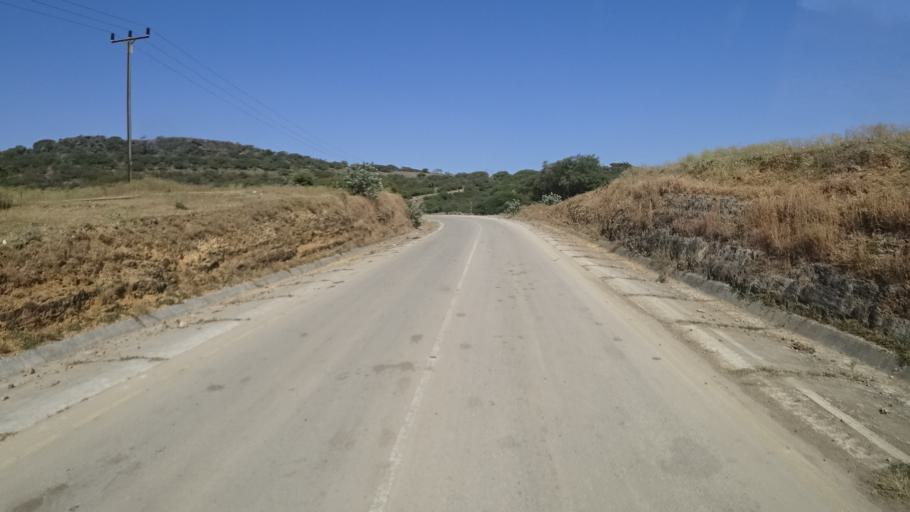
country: OM
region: Zufar
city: Salalah
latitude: 17.0685
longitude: 54.5986
